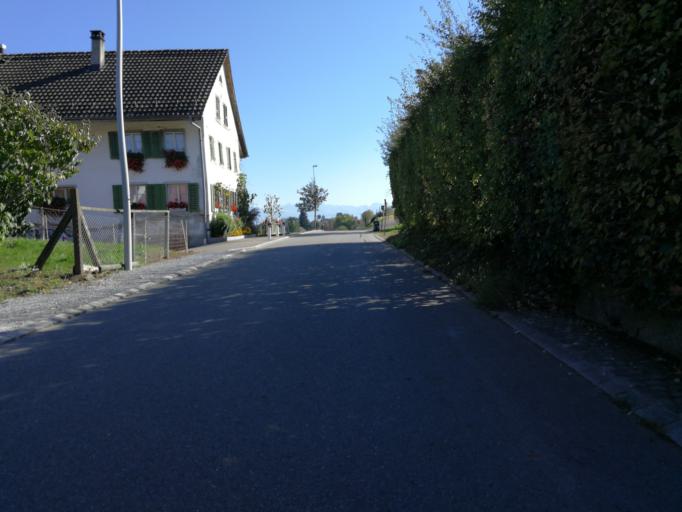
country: CH
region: Zurich
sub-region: Bezirk Uster
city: Aesch
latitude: 47.3220
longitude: 8.6690
